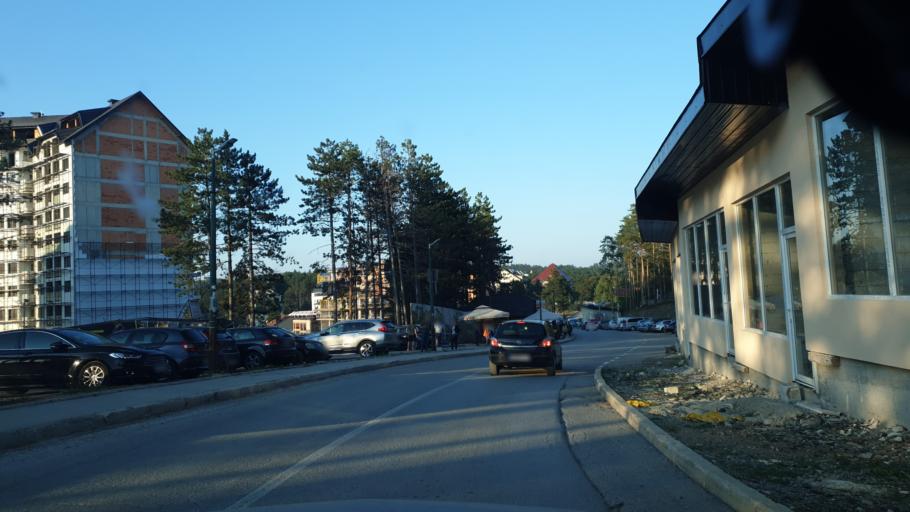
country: RS
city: Zlatibor
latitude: 43.7231
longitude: 19.6957
